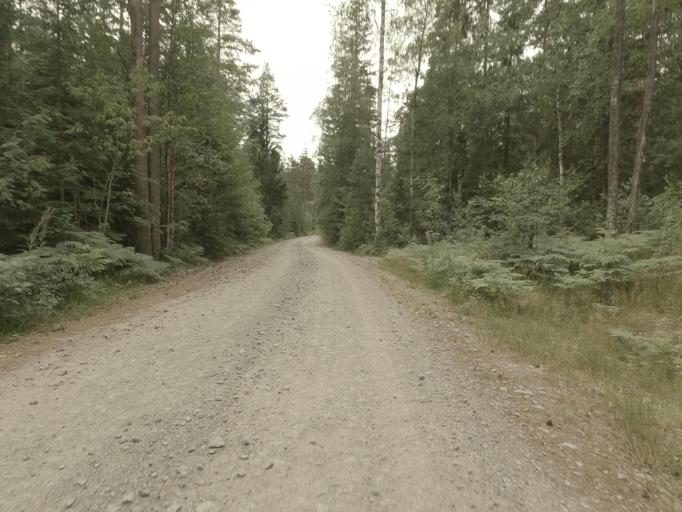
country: RU
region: Leningrad
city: Kamennogorsk
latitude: 60.9873
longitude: 29.1838
